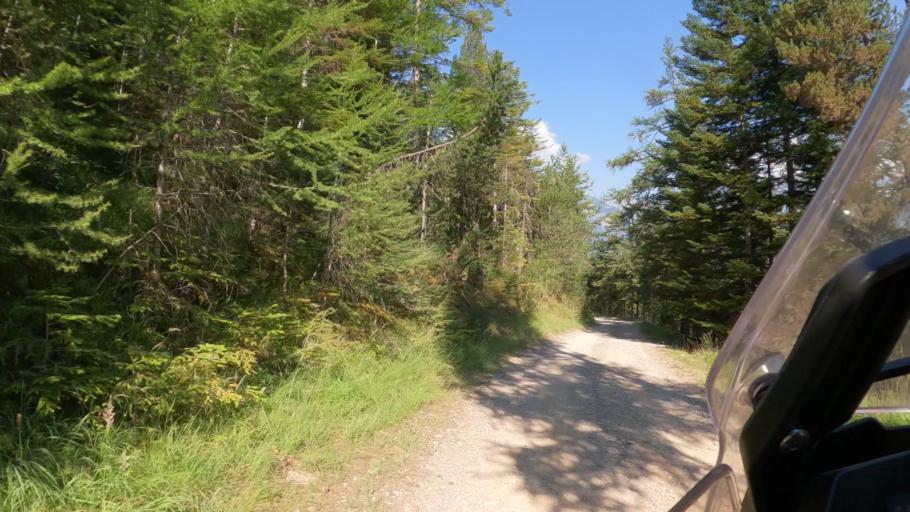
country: FR
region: Provence-Alpes-Cote d'Azur
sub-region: Departement des Hautes-Alpes
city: Embrun
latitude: 44.5883
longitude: 6.5576
